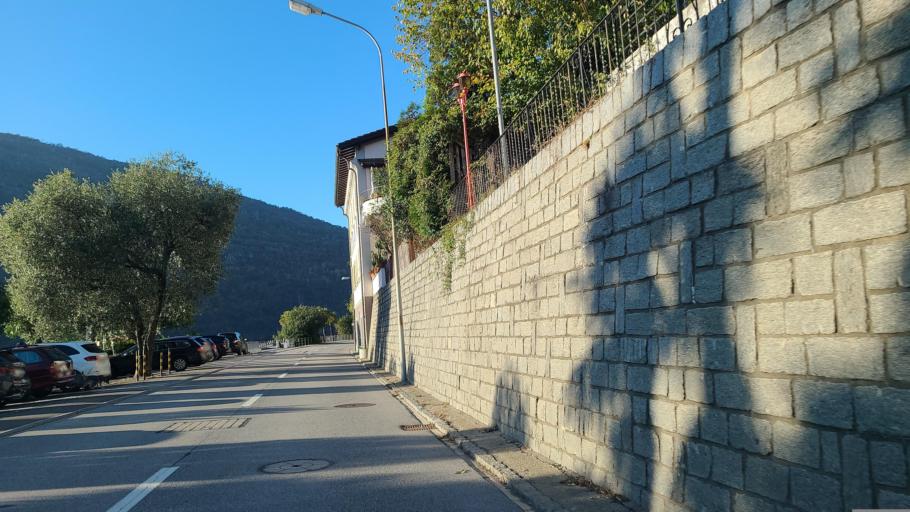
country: IT
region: Lombardy
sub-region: Provincia di Varese
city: Brusimpiano
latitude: 45.9311
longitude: 8.9006
